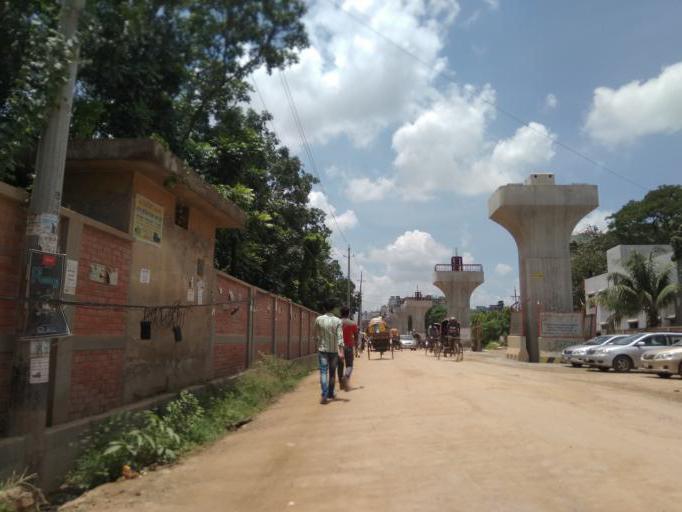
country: BD
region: Dhaka
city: Tungi
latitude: 23.8328
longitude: 90.3638
